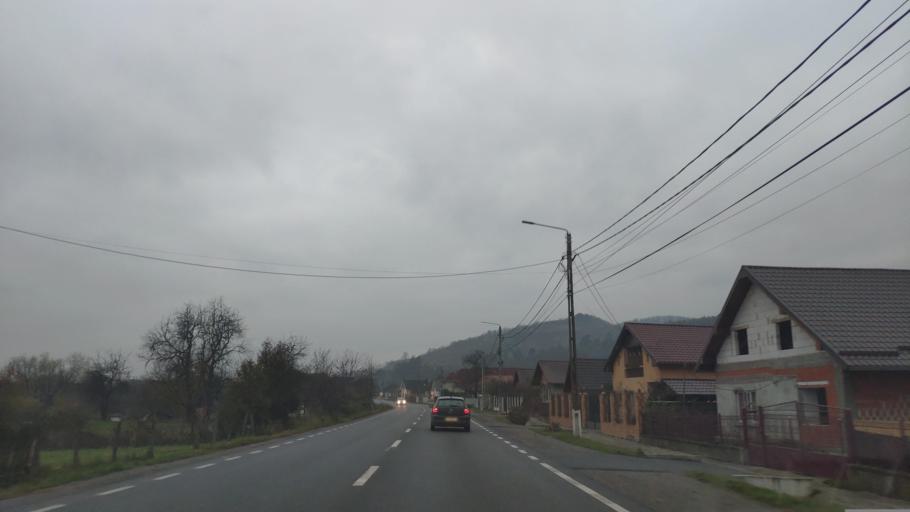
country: RO
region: Maramures
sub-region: Comuna Cicarlau
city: Ilba
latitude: 47.7116
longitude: 23.3628
